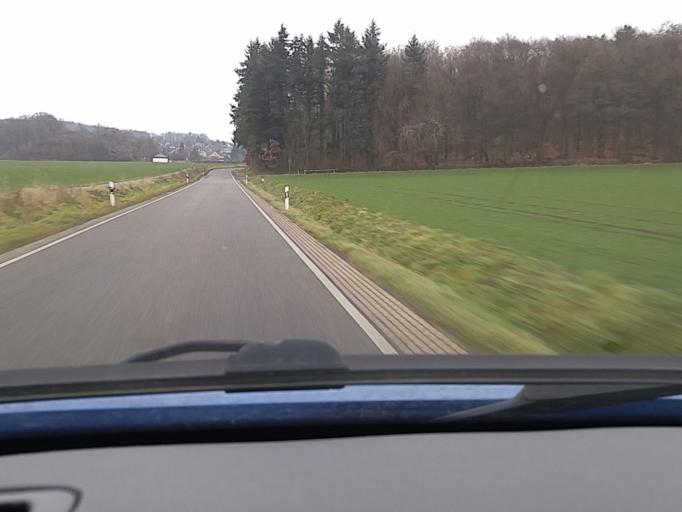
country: DE
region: Hesse
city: Reichelsheim
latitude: 50.3606
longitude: 8.9136
